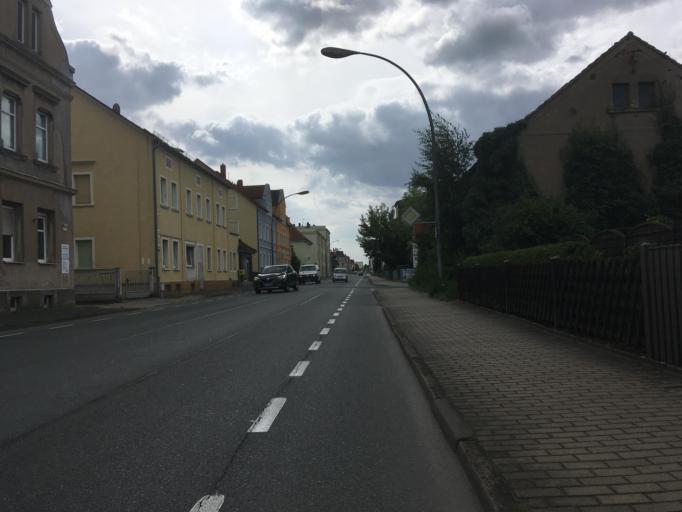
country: DE
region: Saxony
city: Riesa
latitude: 51.3063
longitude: 13.2830
